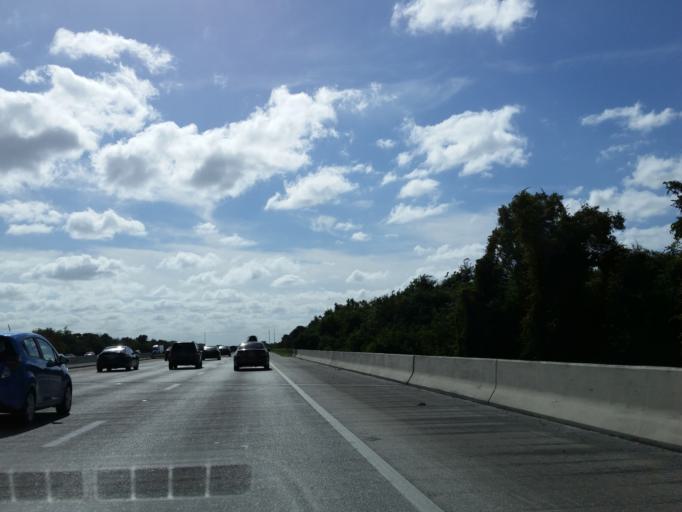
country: US
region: Florida
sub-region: Hillsborough County
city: Riverview
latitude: 27.8448
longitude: -82.3478
